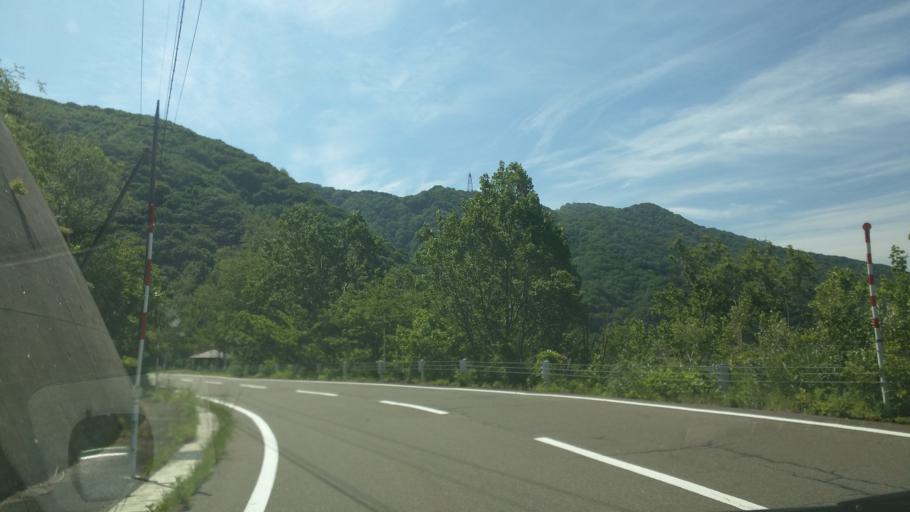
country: JP
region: Fukushima
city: Kitakata
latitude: 37.3526
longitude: 139.8723
